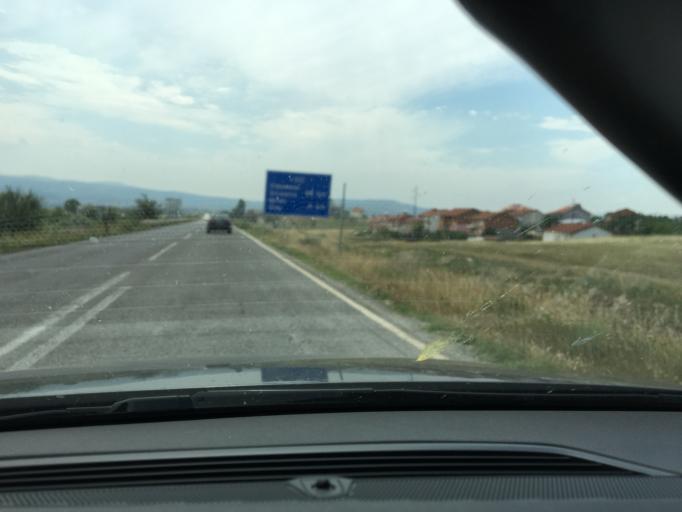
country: MK
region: Stip
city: Shtip
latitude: 41.7774
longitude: 22.1326
